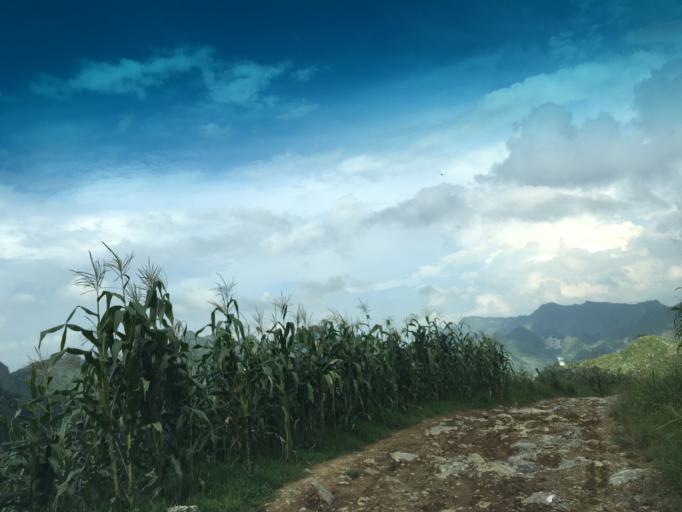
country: CN
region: Guangxi Zhuangzu Zizhiqu
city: Xinzhou
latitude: 24.9918
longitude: 105.6361
